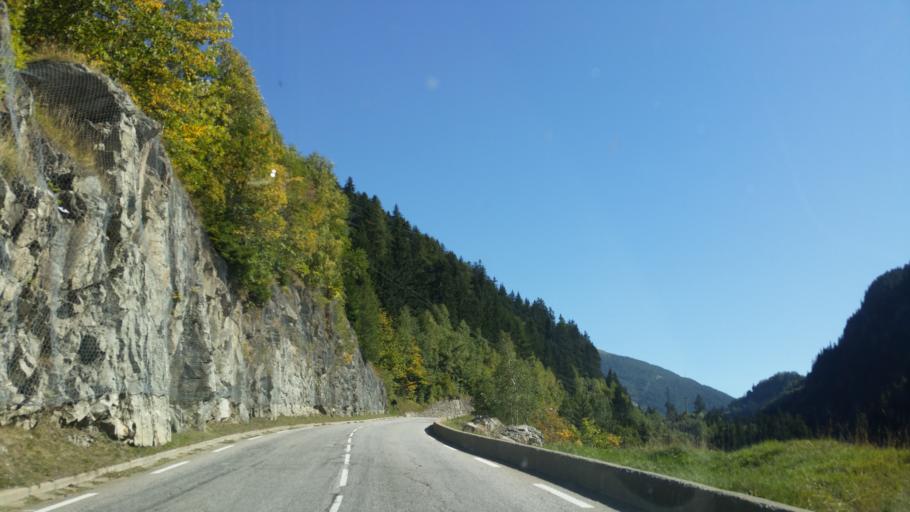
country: FR
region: Rhone-Alpes
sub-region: Departement de la Savoie
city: Tignes
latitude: 45.5669
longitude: 6.8894
